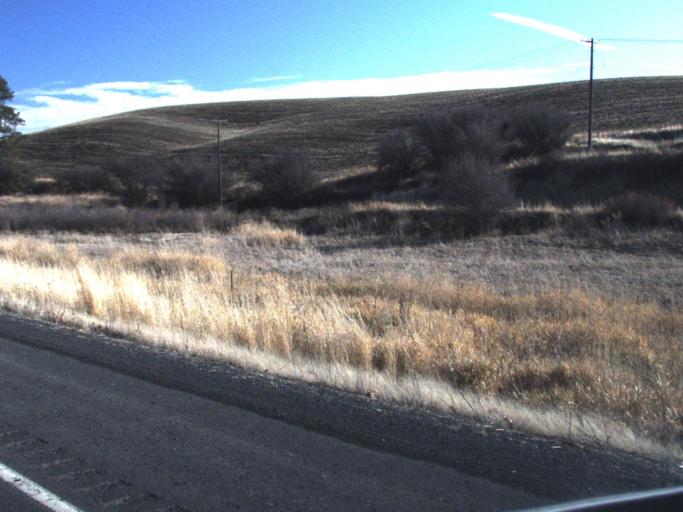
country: US
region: Washington
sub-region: Whitman County
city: Pullman
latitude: 46.7247
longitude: -117.1246
